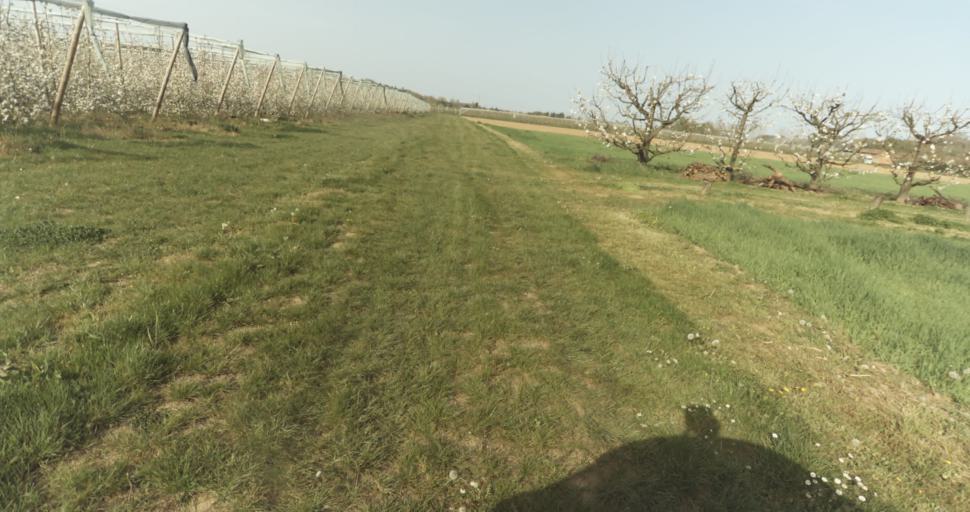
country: FR
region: Midi-Pyrenees
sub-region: Departement du Tarn-et-Garonne
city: Moissac
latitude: 44.1126
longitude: 1.1397
